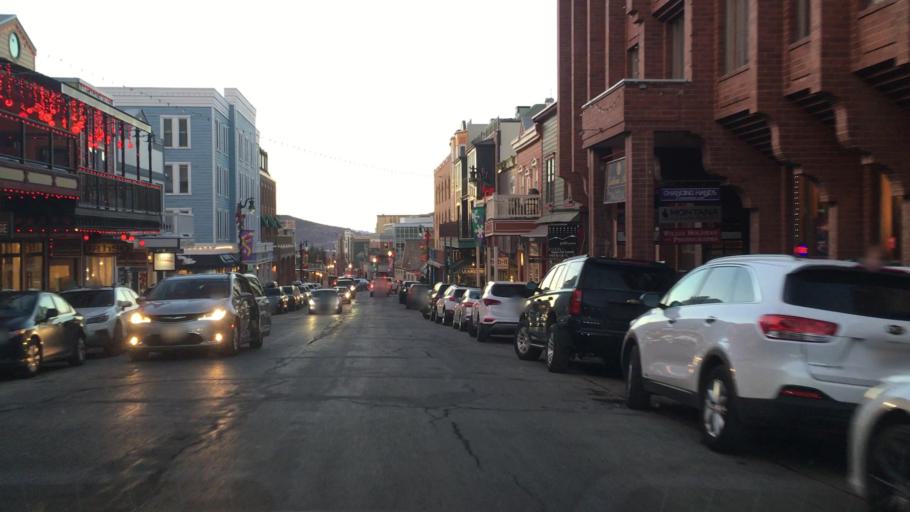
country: US
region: Utah
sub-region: Summit County
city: Park City
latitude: 40.6453
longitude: -111.4967
